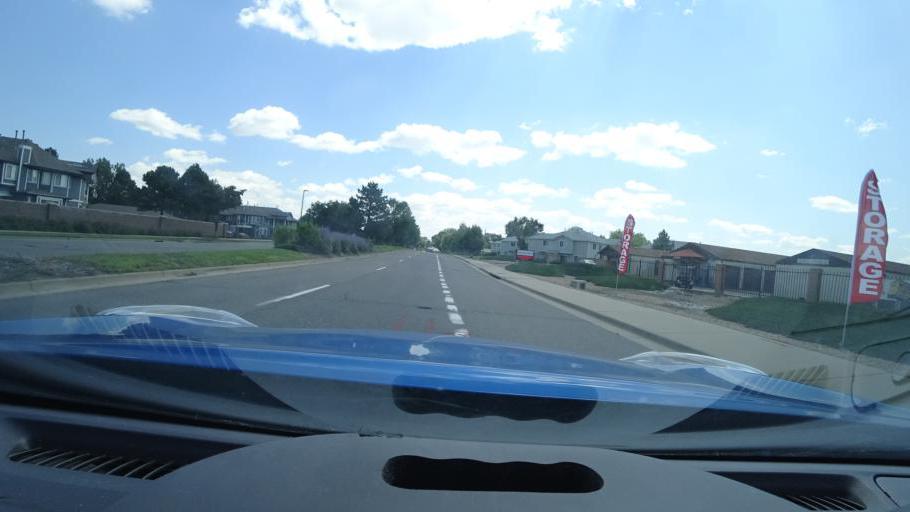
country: US
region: Colorado
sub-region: Arapahoe County
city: Glendale
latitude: 39.6965
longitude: -104.8878
